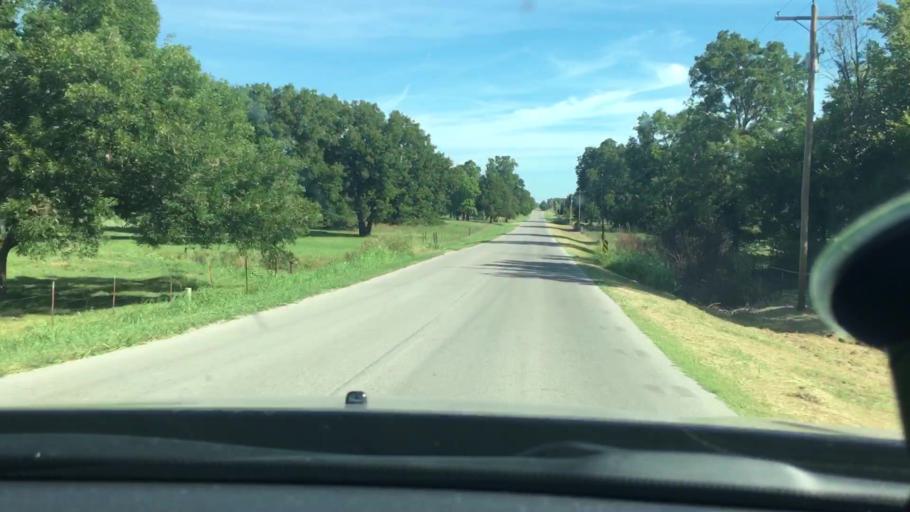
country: US
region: Oklahoma
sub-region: Carter County
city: Lone Grove
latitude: 34.2384
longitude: -97.2474
